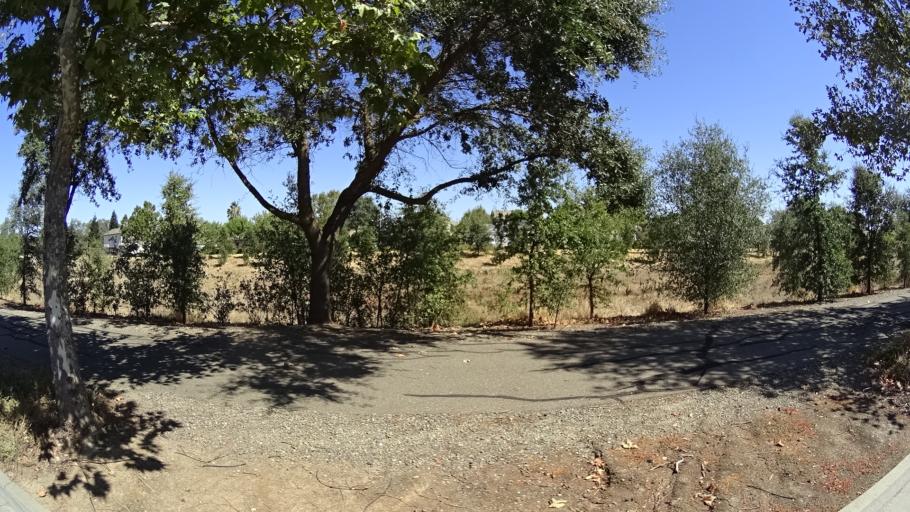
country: US
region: California
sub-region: Sacramento County
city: Elk Grove
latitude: 38.4222
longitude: -121.3479
